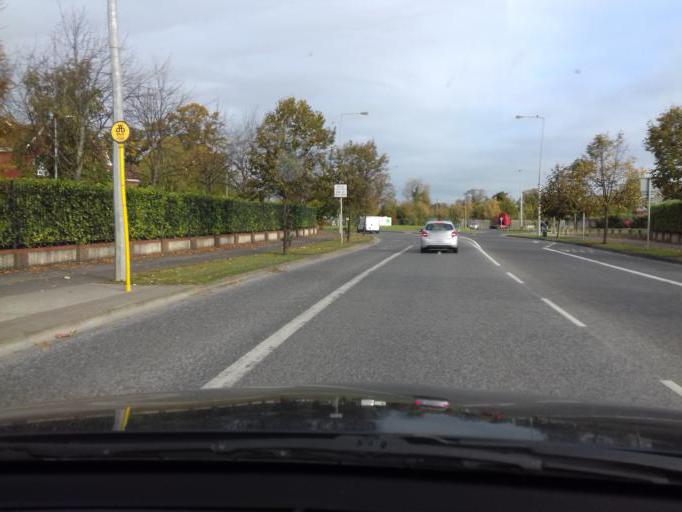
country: IE
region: Leinster
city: Hartstown
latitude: 53.3979
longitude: -6.4423
